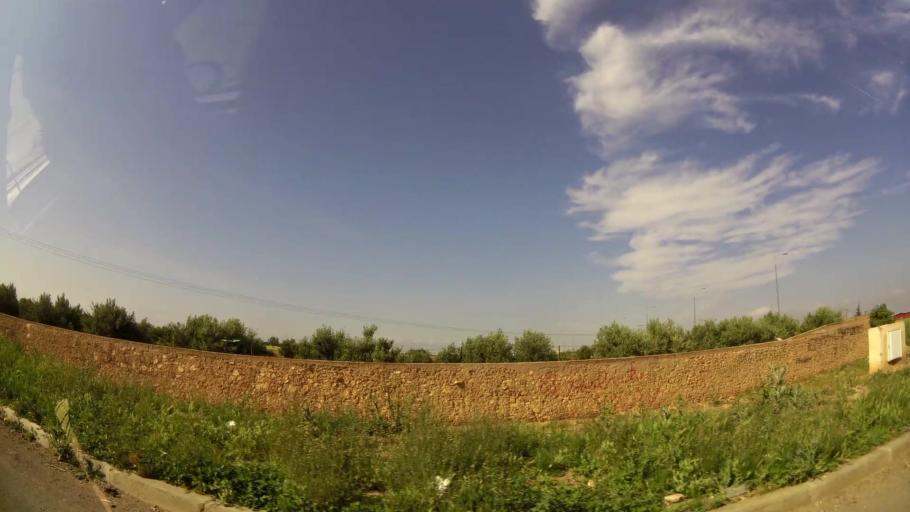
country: MA
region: Oriental
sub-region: Oujda-Angad
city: Oujda
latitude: 34.7244
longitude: -1.8786
